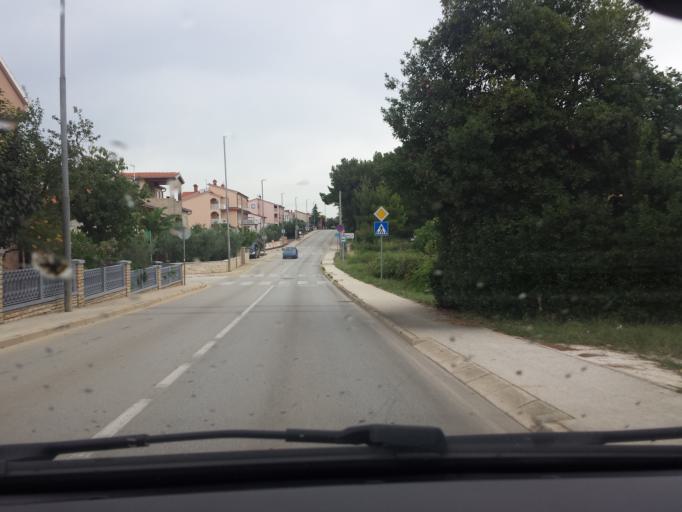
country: HR
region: Istarska
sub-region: Grad Pula
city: Pula
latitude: 44.8952
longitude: 13.8505
